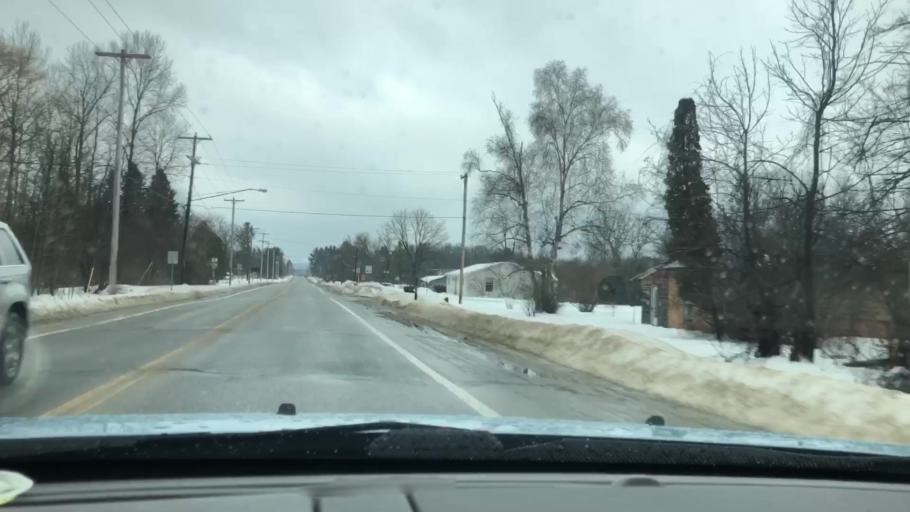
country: US
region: Michigan
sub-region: Charlevoix County
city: East Jordan
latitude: 45.1510
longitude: -85.1192
